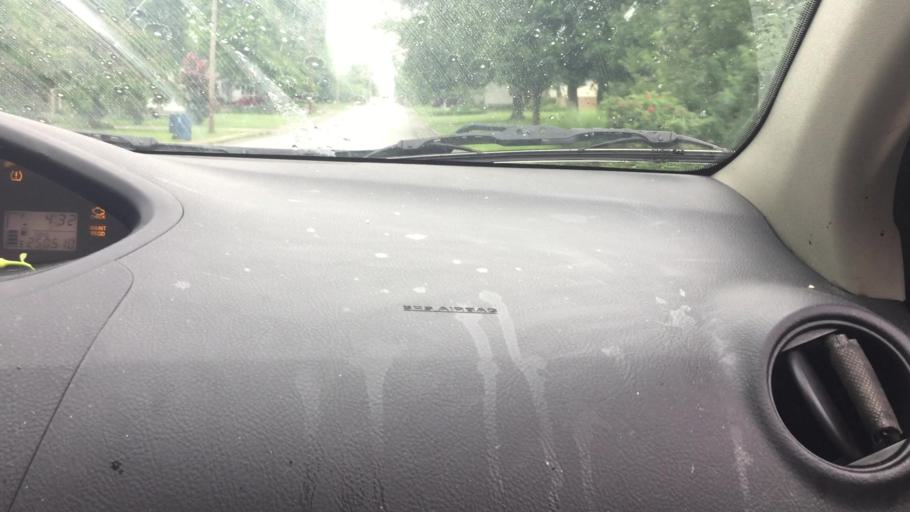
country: US
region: Illinois
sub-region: Williamson County
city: Marion
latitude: 37.7228
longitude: -88.9463
